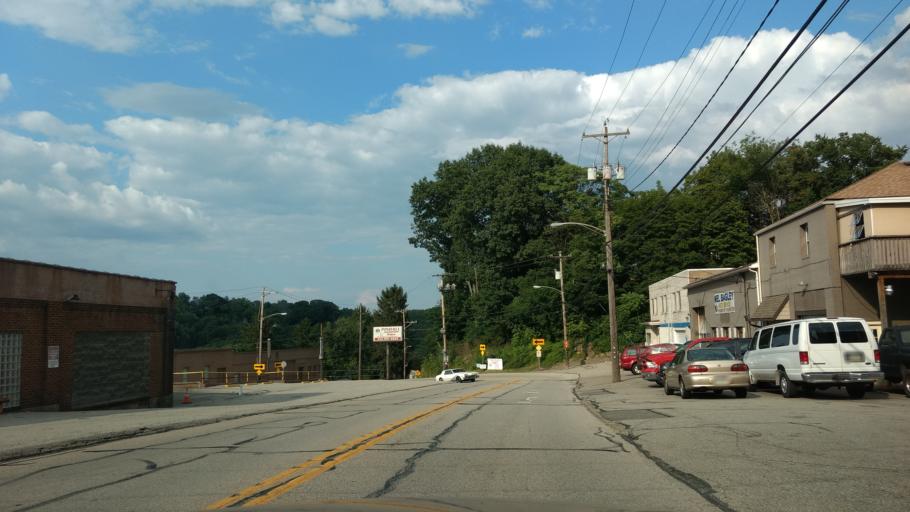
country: US
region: Pennsylvania
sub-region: Allegheny County
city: West View
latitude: 40.5182
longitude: -80.0268
